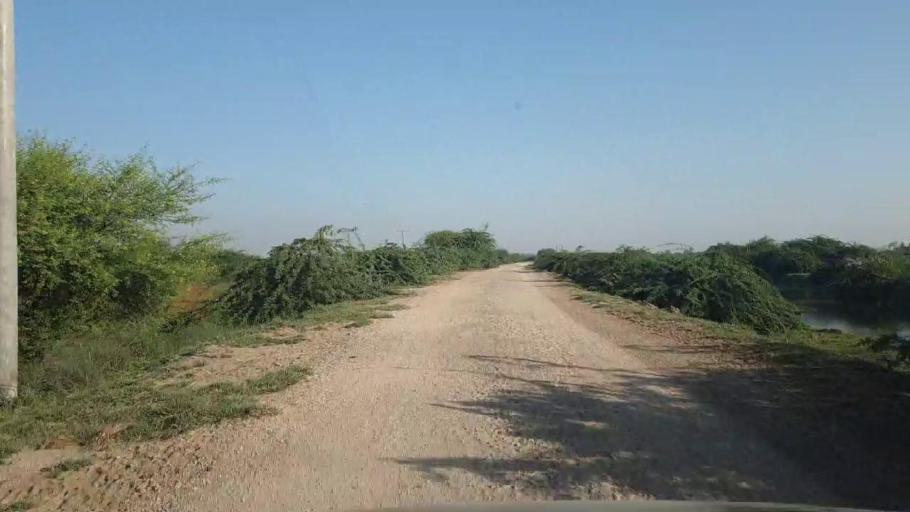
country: PK
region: Sindh
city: Badin
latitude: 24.6946
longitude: 68.8160
